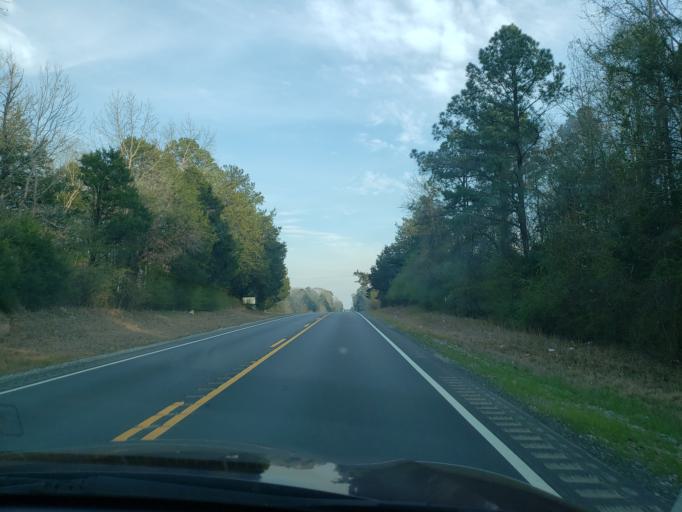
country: US
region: Alabama
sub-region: Hale County
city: Moundville
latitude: 32.8991
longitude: -87.6267
